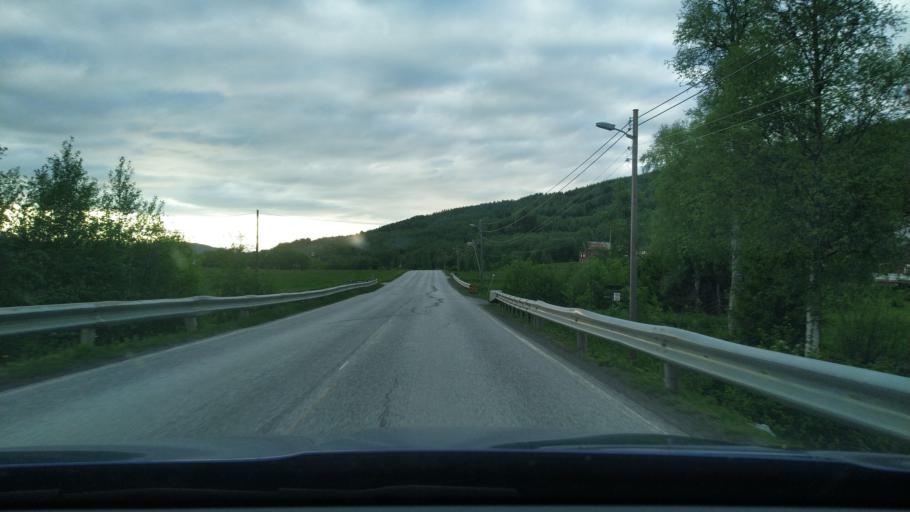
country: NO
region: Troms
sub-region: Sorreisa
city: Sorreisa
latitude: 69.1242
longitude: 18.2169
